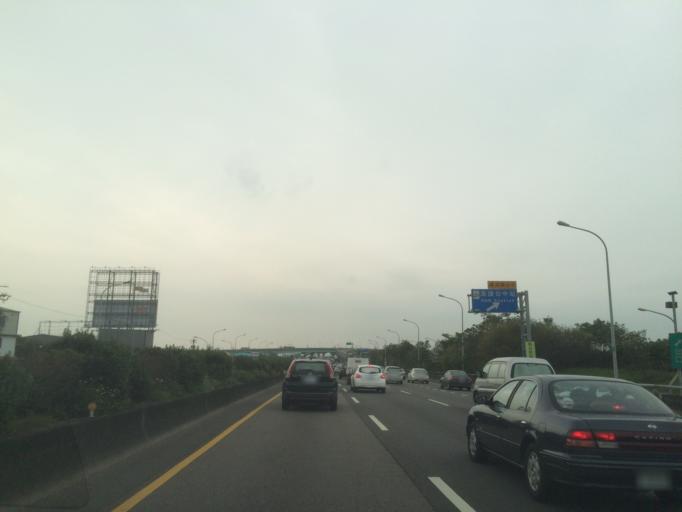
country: TW
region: Taiwan
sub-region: Taichung City
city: Taichung
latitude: 24.1254
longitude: 120.6198
